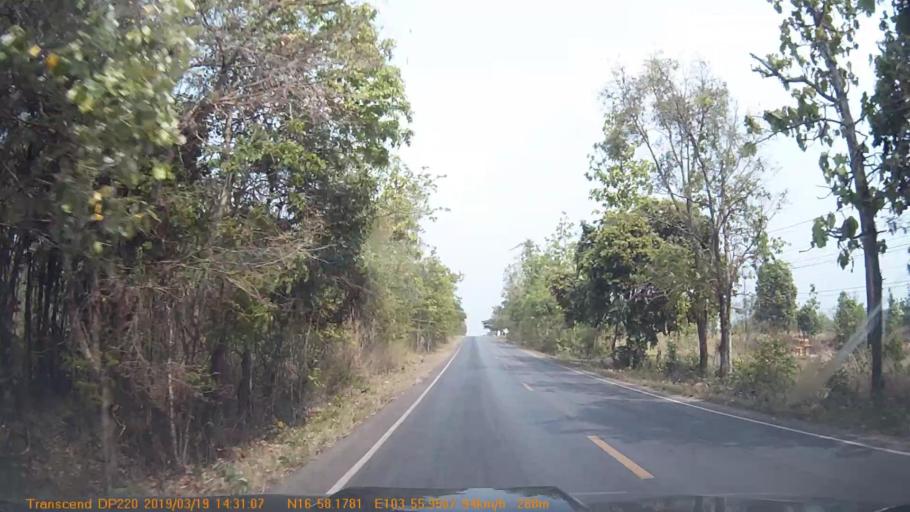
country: TH
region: Sakon Nakhon
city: Phu Phan
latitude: 16.9695
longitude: 103.9333
